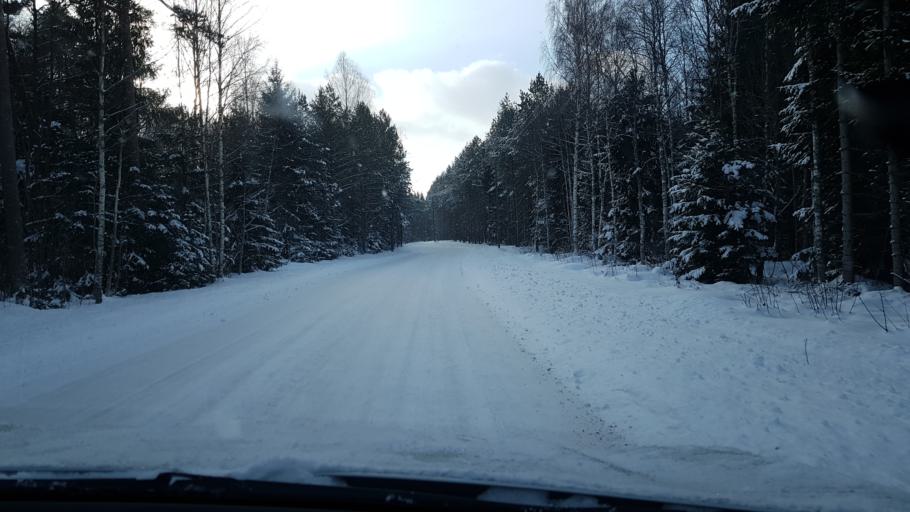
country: EE
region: Harju
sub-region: Nissi vald
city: Turba
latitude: 59.1794
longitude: 24.1334
